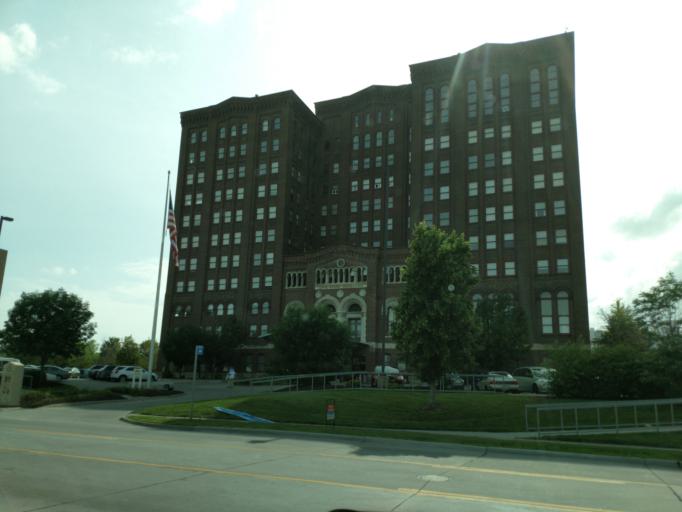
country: US
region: Nebraska
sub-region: Douglas County
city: Omaha
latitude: 41.2101
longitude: -95.9550
